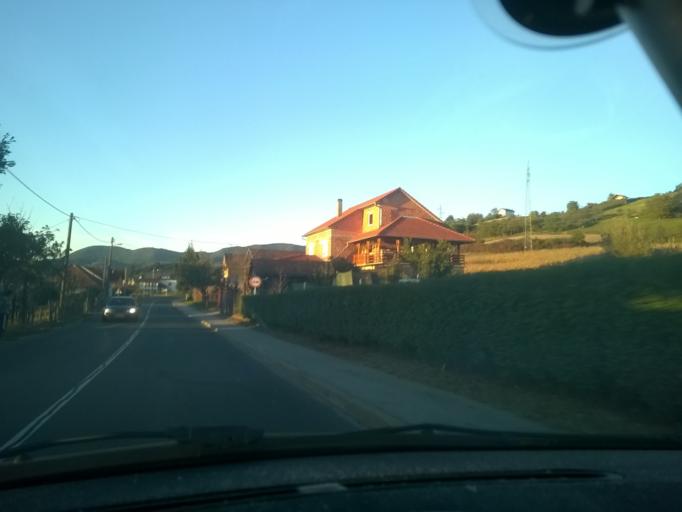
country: HR
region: Krapinsko-Zagorska
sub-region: Grad Krapina
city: Krapina
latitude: 46.1191
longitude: 15.8945
